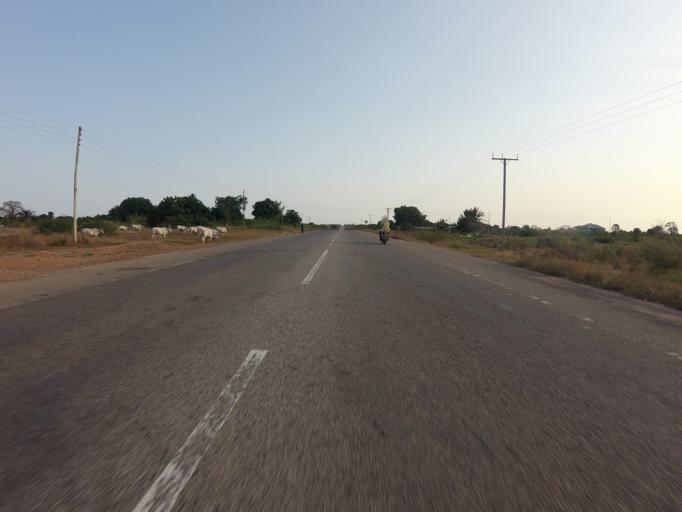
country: GH
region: Volta
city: Anloga
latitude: 6.0302
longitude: 0.6033
